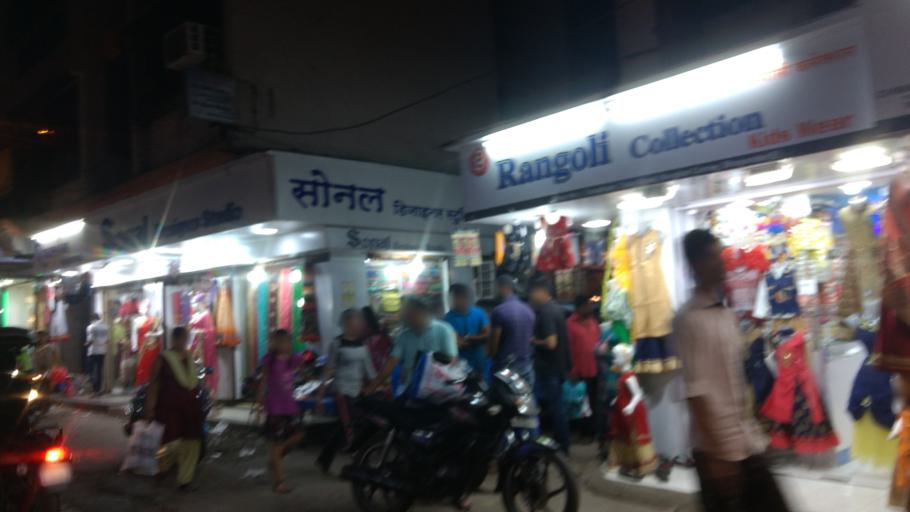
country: IN
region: Maharashtra
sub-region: Thane
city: Bhayandar
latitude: 19.3095
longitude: 72.8584
